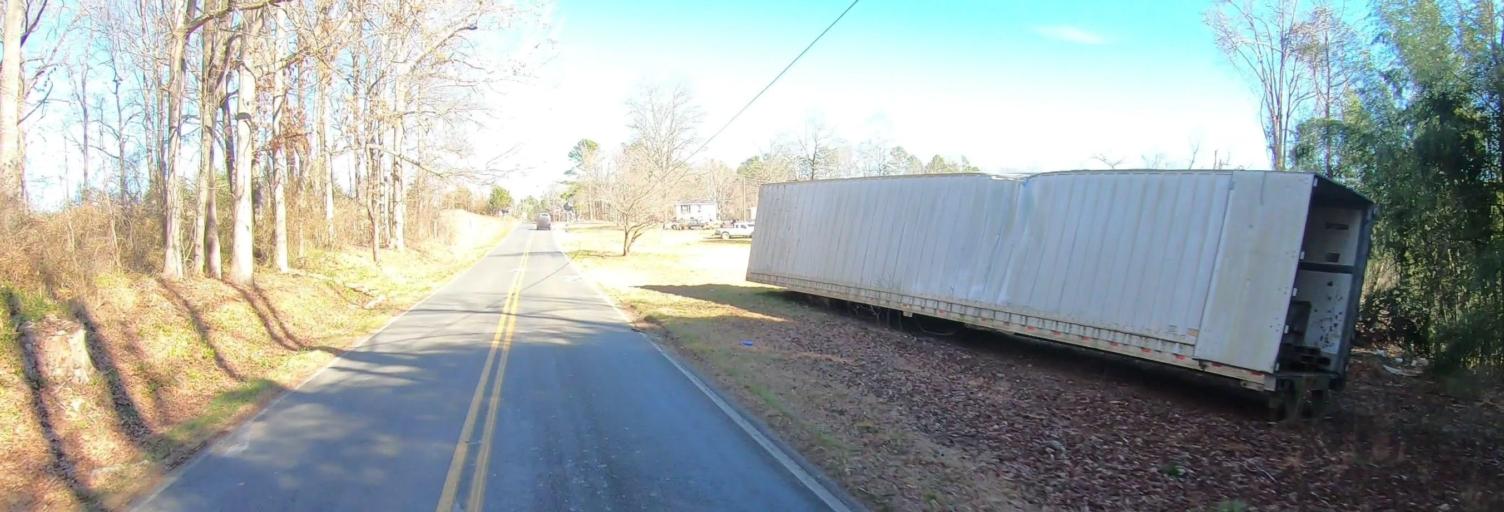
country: US
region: South Carolina
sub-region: Oconee County
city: Walhalla
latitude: 34.7243
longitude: -83.0621
